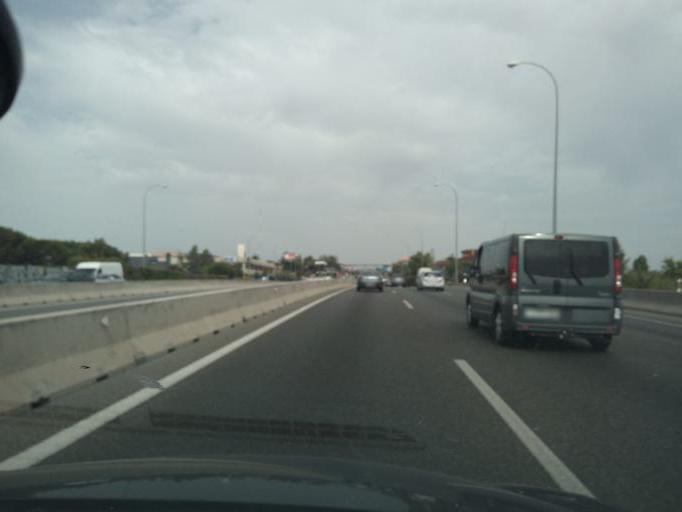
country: ES
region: Madrid
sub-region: Provincia de Madrid
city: Majadahonda
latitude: 40.4804
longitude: -3.8507
